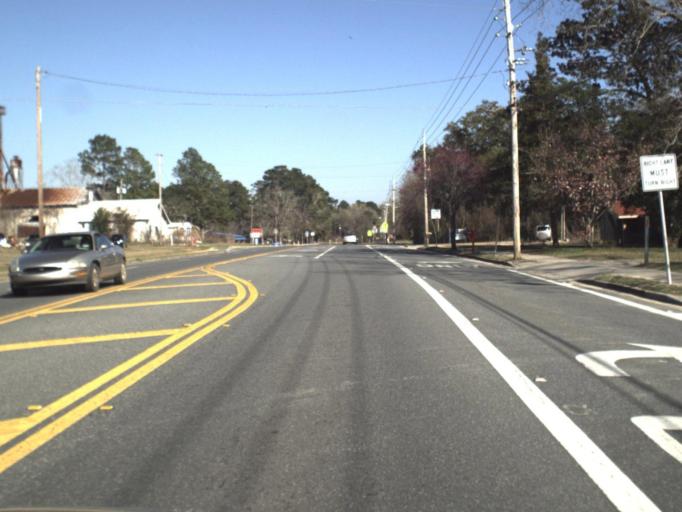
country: US
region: Florida
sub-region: Jackson County
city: Marianna
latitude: 30.7923
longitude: -85.3696
